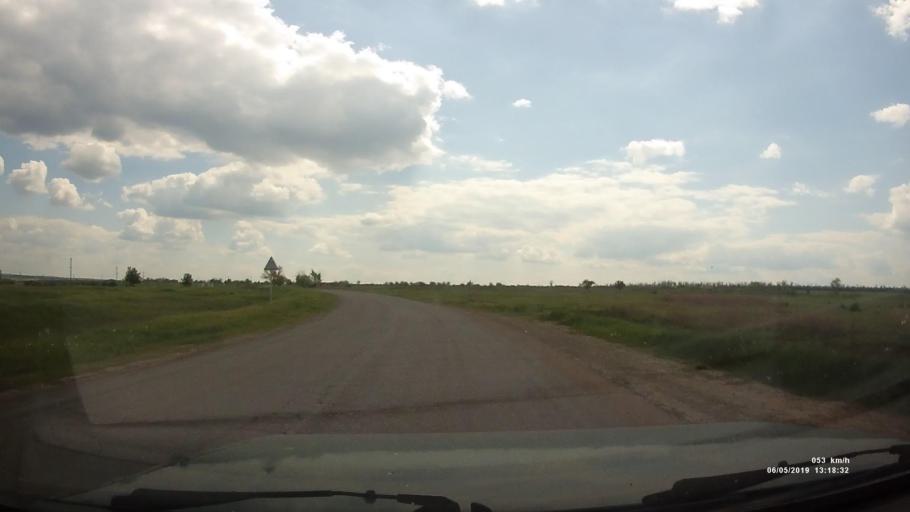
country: RU
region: Rostov
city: Ust'-Donetskiy
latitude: 47.7334
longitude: 40.9135
